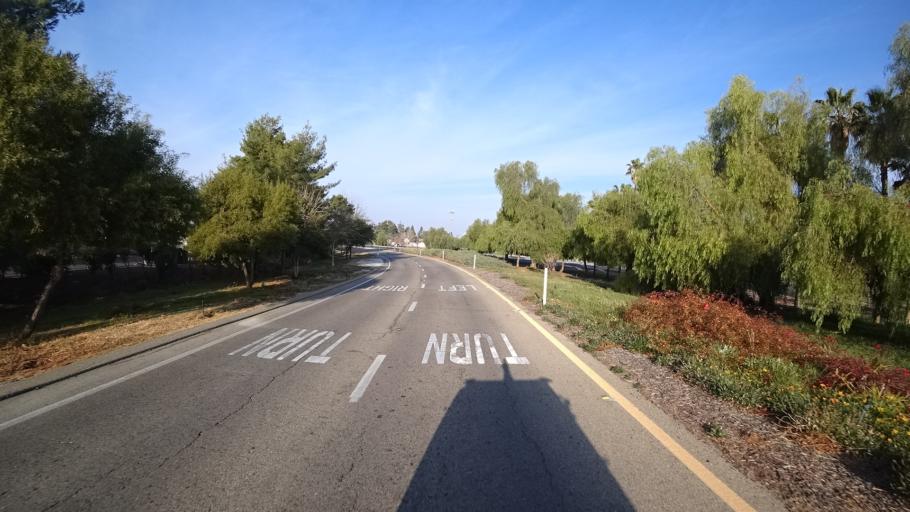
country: US
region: California
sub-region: Kern County
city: Bakersfield
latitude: 35.3955
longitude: -118.9513
